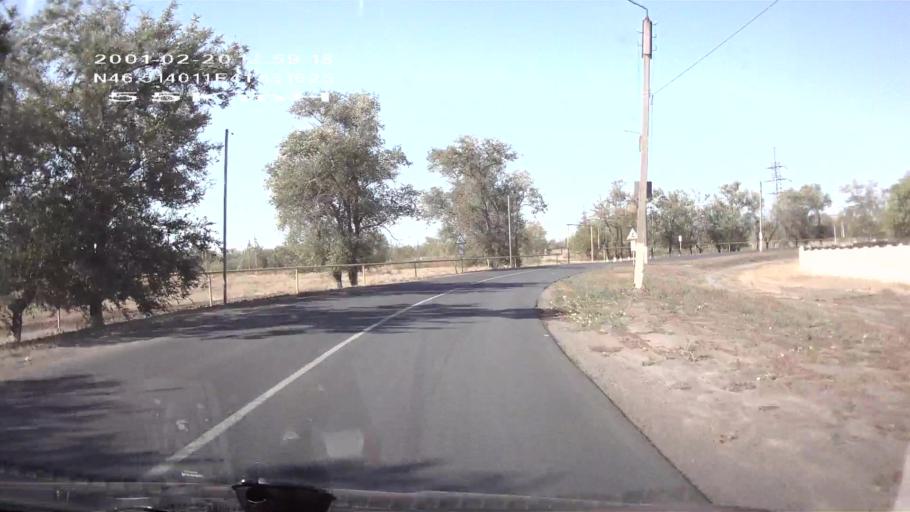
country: RU
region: Rostov
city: Gigant
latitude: 46.5141
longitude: 41.3314
